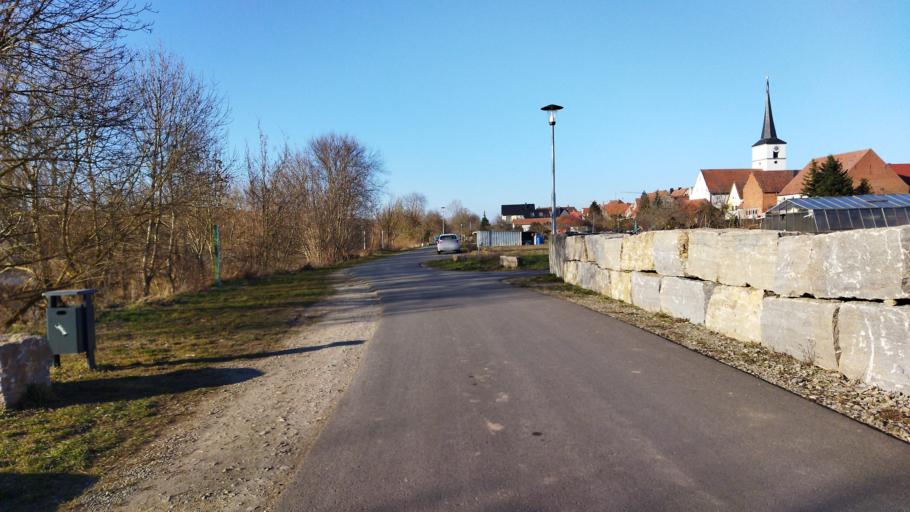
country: DE
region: Bavaria
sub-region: Regierungsbezirk Unterfranken
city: Albertshofen
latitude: 49.7692
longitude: 10.1580
